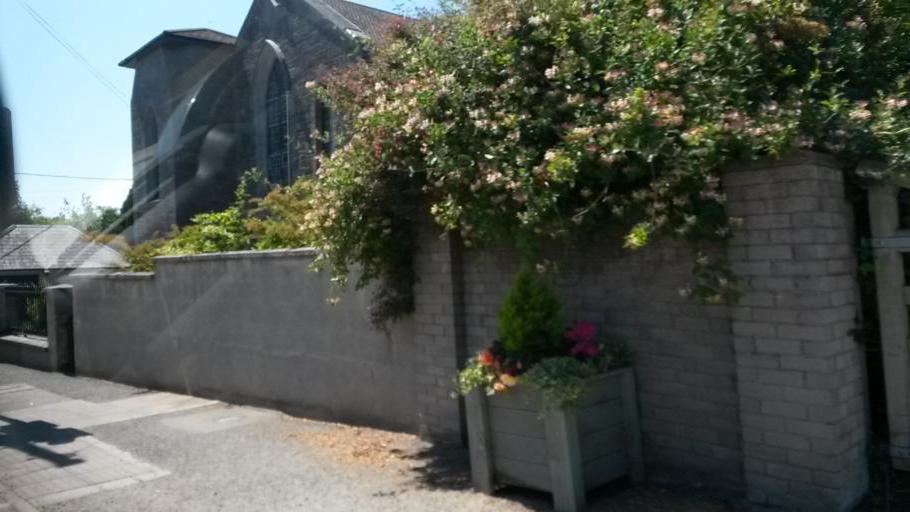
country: IE
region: Leinster
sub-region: Fingal County
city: Swords
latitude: 53.5212
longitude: -6.2673
